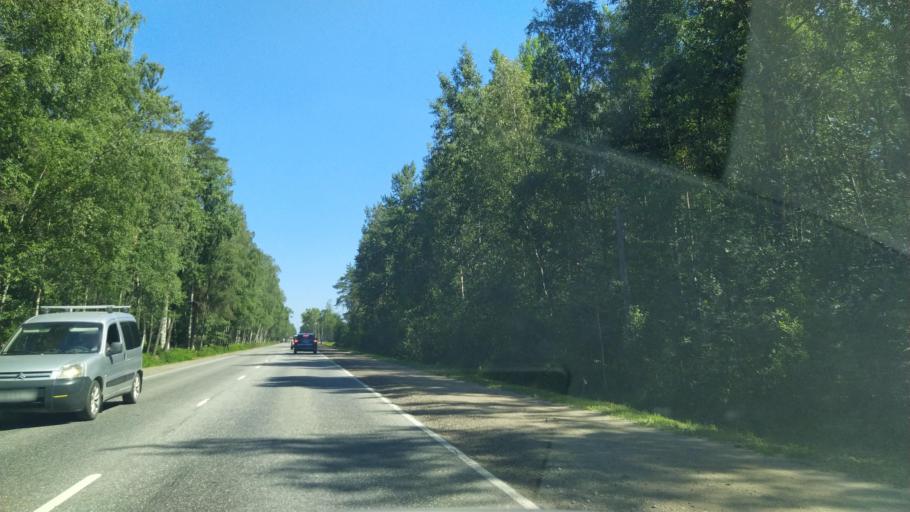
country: RU
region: Leningrad
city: Imeni Morozova
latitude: 59.9650
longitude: 31.0136
